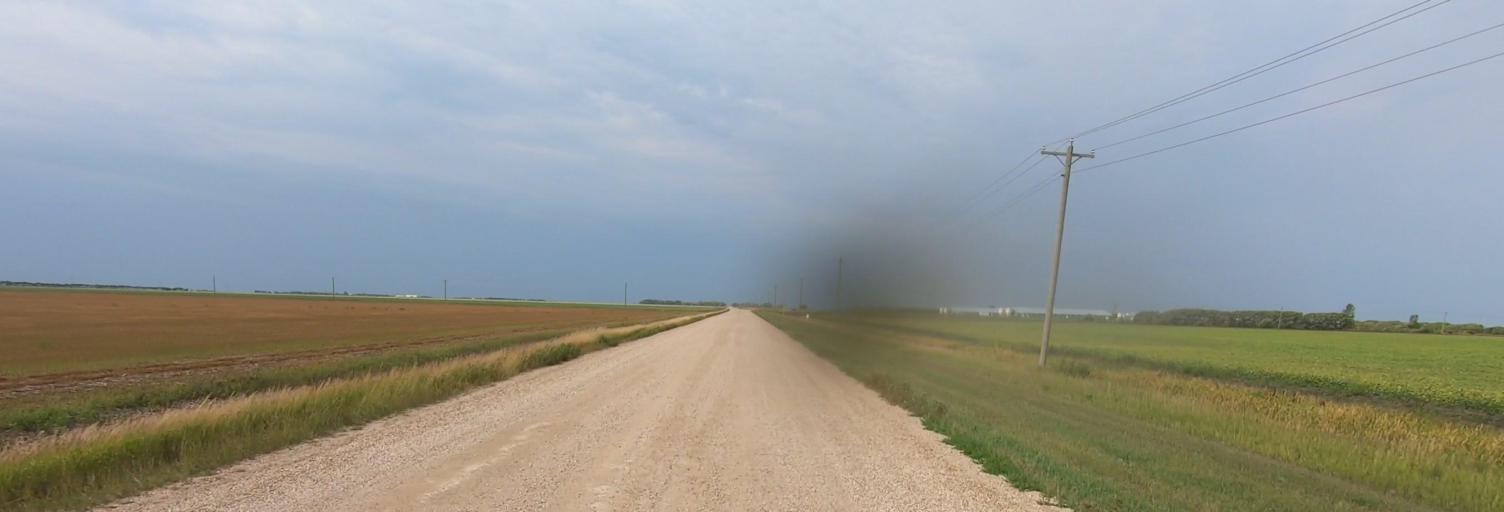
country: CA
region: Manitoba
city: Morris
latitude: 49.5764
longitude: -97.3173
